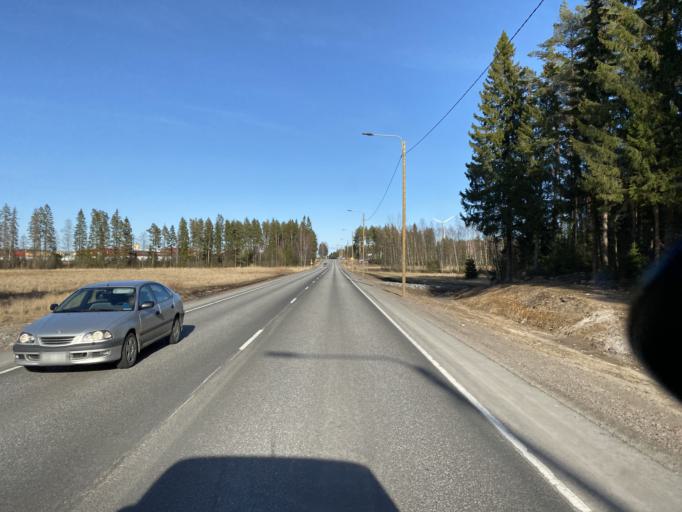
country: FI
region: Satakunta
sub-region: Rauma
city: Eura
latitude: 61.1456
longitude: 22.2115
